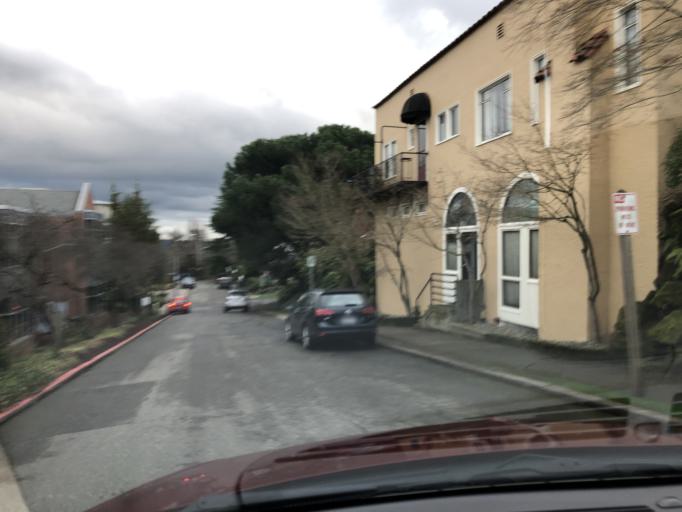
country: US
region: Washington
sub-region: King County
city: Seattle
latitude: 47.6409
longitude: -122.3179
